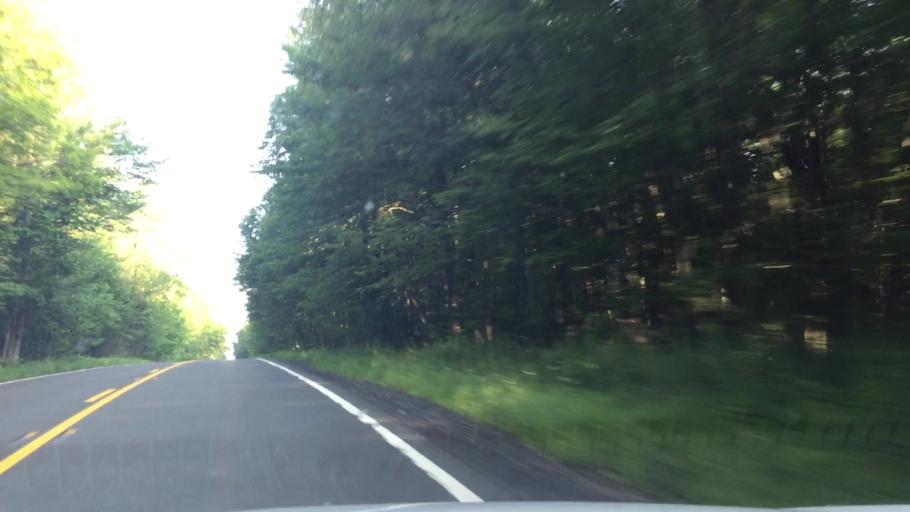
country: US
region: Massachusetts
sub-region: Berkshire County
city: Hinsdale
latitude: 42.3846
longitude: -73.1573
